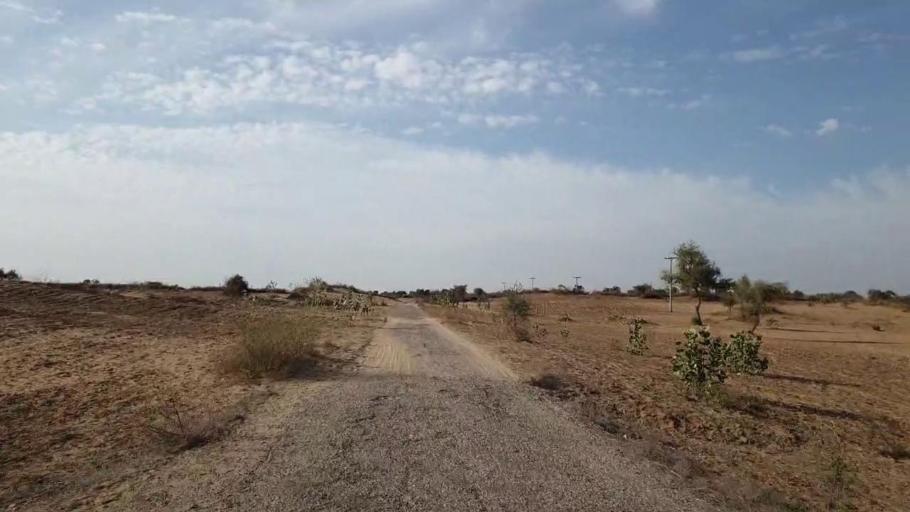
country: PK
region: Sindh
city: Nabisar
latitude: 25.0510
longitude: 69.9692
